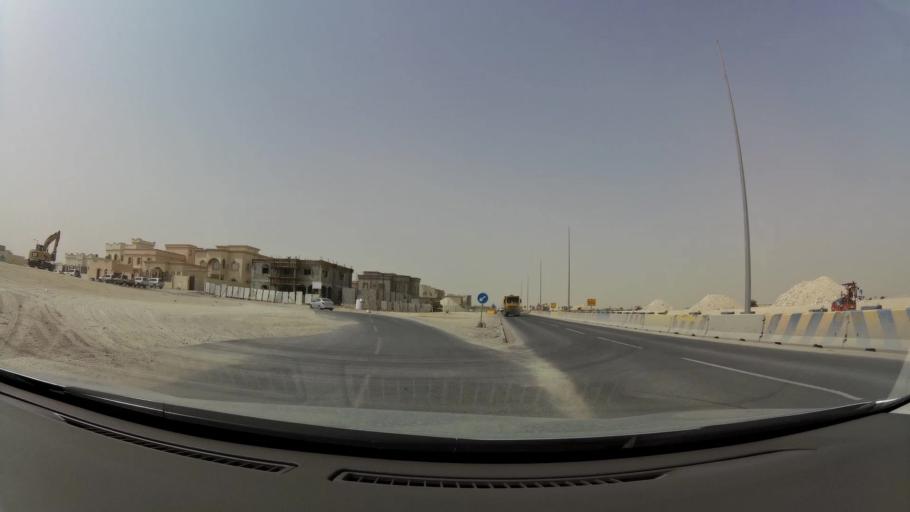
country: QA
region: Baladiyat ar Rayyan
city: Ar Rayyan
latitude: 25.2611
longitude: 51.3754
